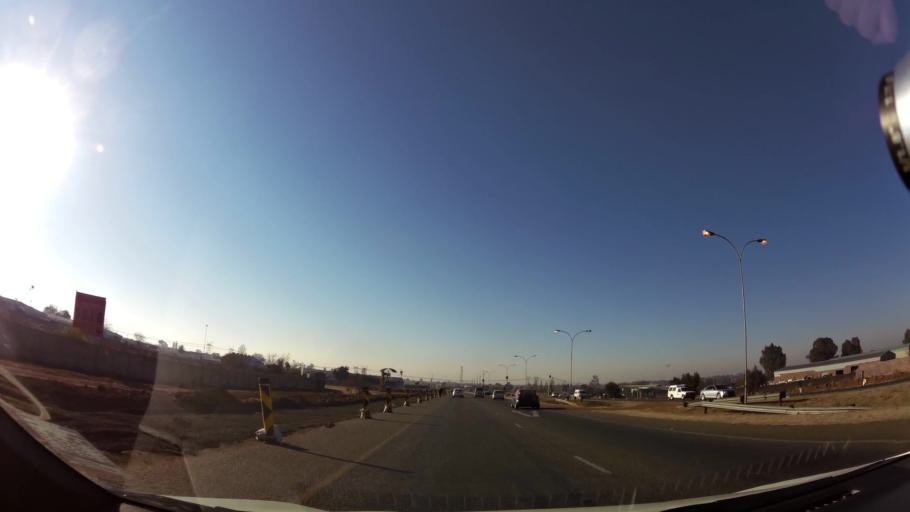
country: ZA
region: Gauteng
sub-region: Ekurhuleni Metropolitan Municipality
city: Germiston
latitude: -26.3576
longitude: 28.1144
